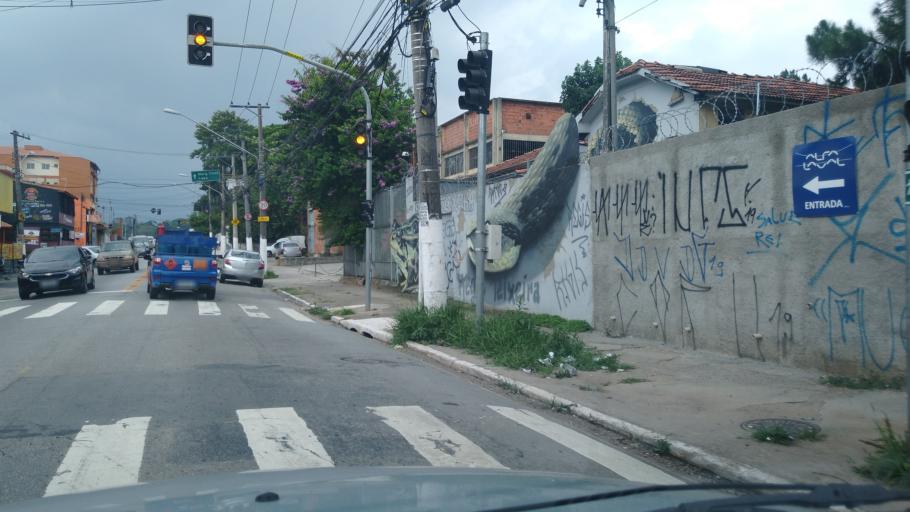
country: BR
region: Sao Paulo
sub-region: Osasco
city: Osasco
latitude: -23.5034
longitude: -46.7576
